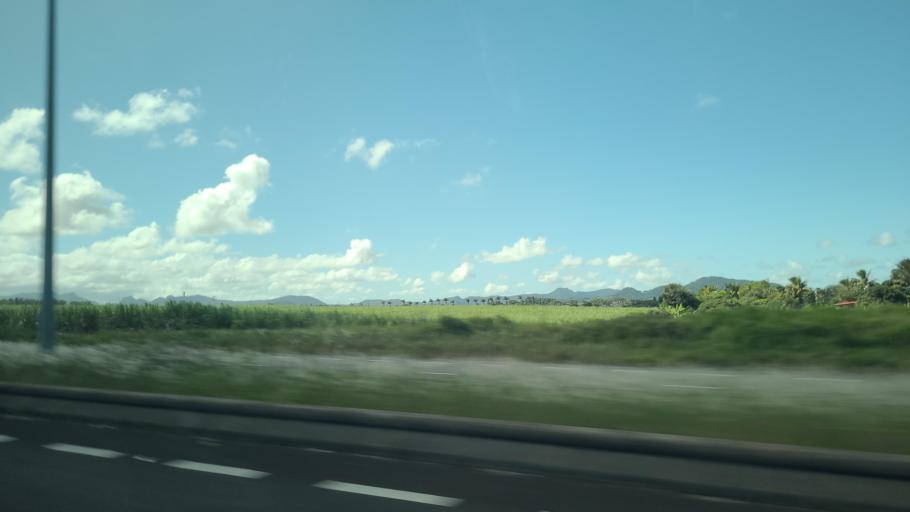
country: MU
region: Grand Port
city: Plaine Magnien
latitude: -20.4386
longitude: 57.6544
